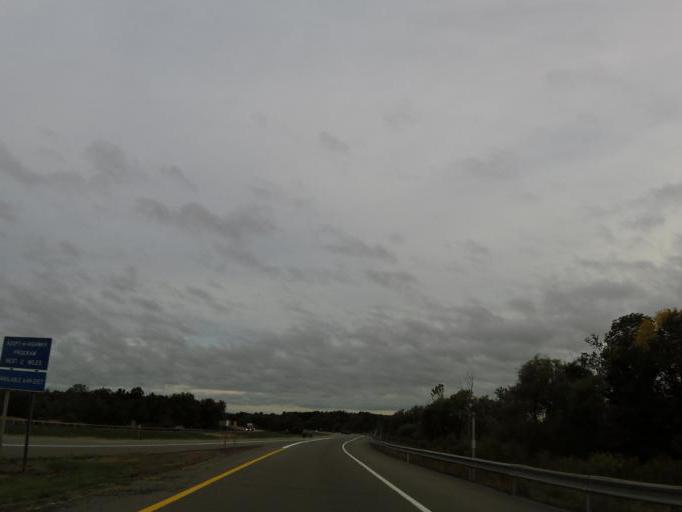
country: US
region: New York
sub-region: Erie County
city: Elma Center
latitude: 42.8069
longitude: -78.6420
